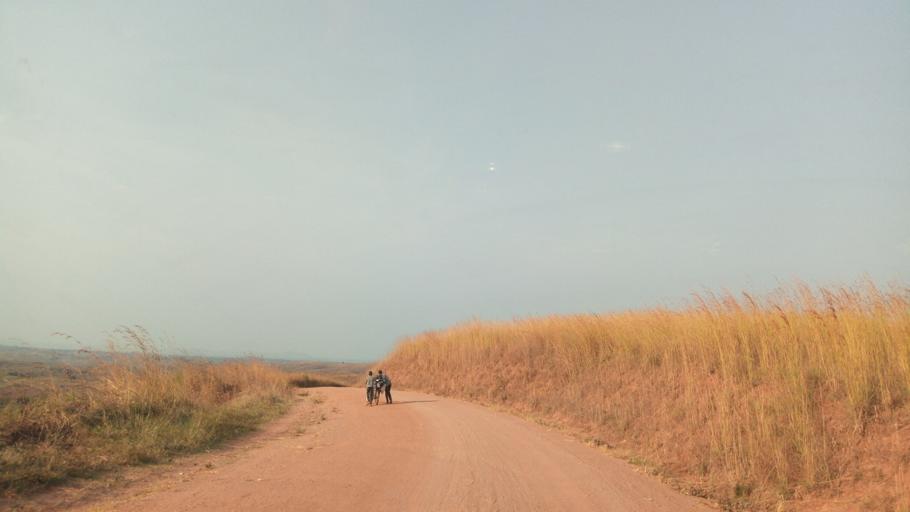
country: CD
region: Katanga
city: Kalemie
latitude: -5.9472
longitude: 29.1426
